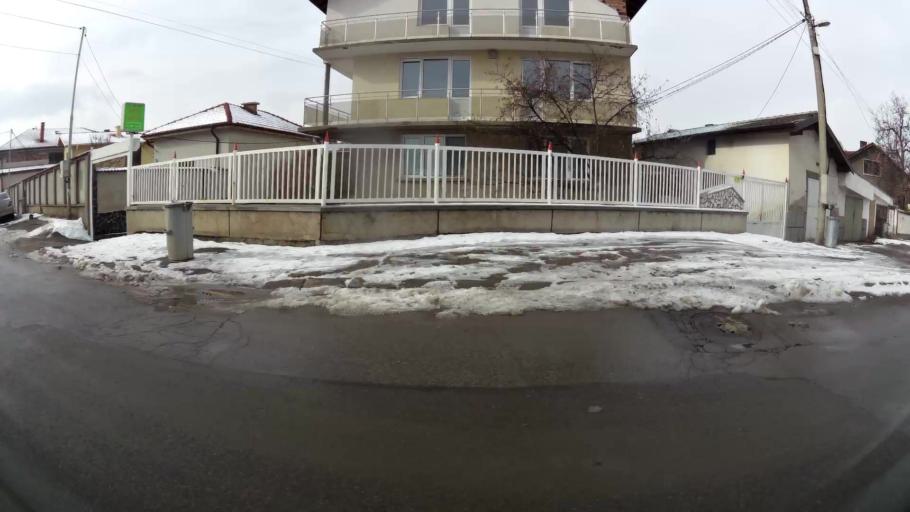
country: BG
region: Sofia-Capital
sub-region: Stolichna Obshtina
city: Sofia
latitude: 42.7123
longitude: 23.4200
